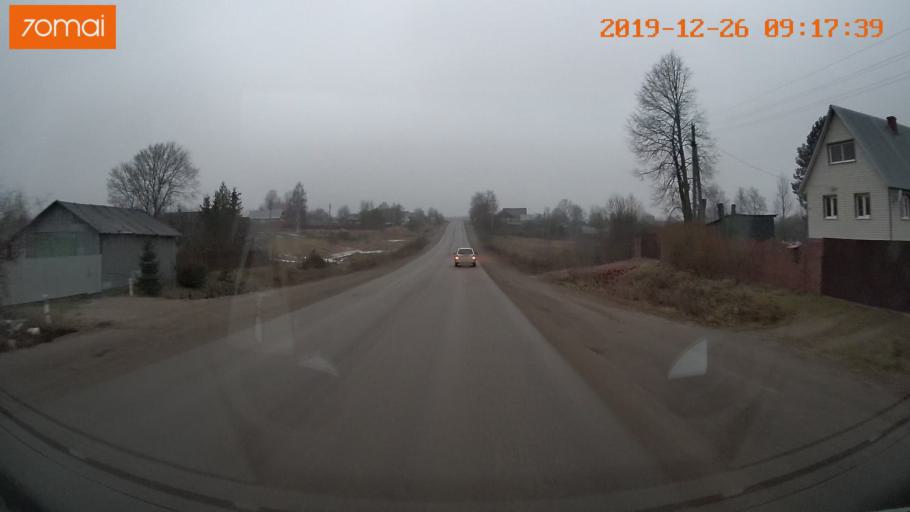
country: RU
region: Vologda
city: Gryazovets
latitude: 58.9317
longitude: 40.2407
